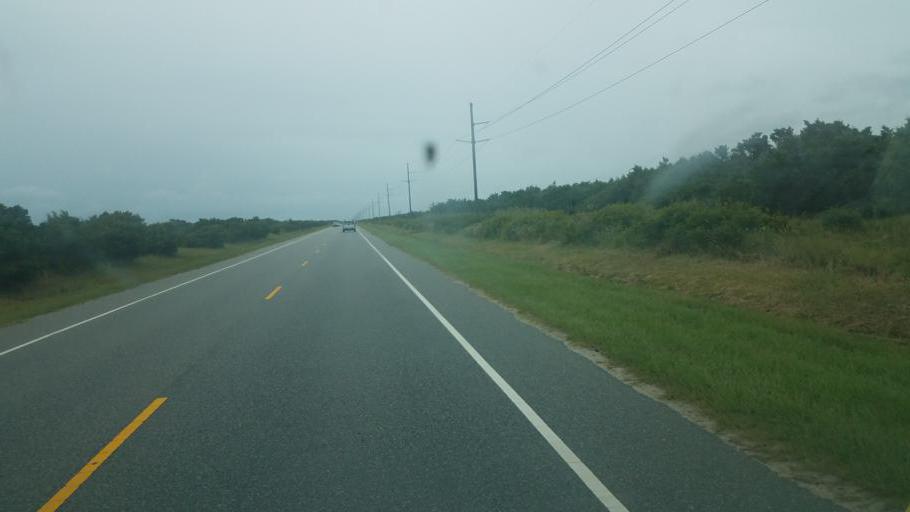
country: US
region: North Carolina
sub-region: Dare County
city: Buxton
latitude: 35.4852
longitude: -75.4816
